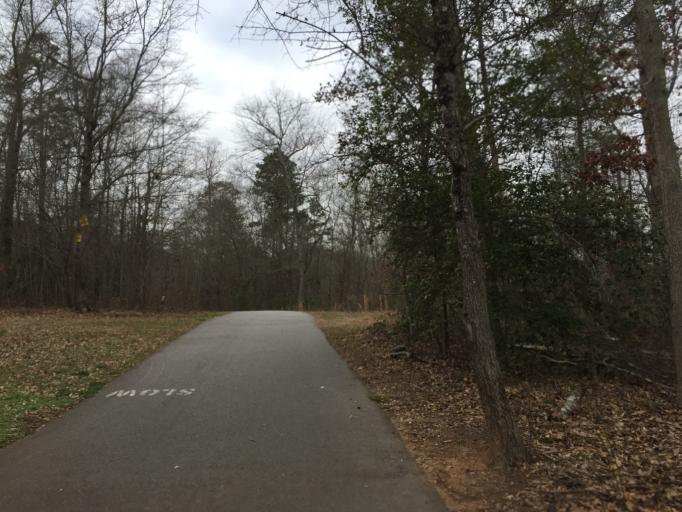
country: US
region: South Carolina
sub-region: Greenville County
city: Mauldin
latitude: 34.7745
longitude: -82.3562
